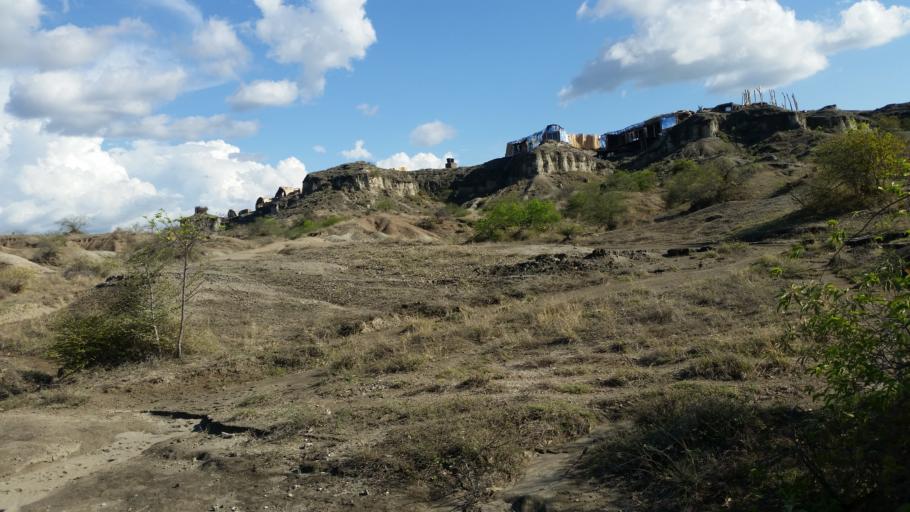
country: CO
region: Huila
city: Villavieja
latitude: 3.2544
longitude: -75.1340
